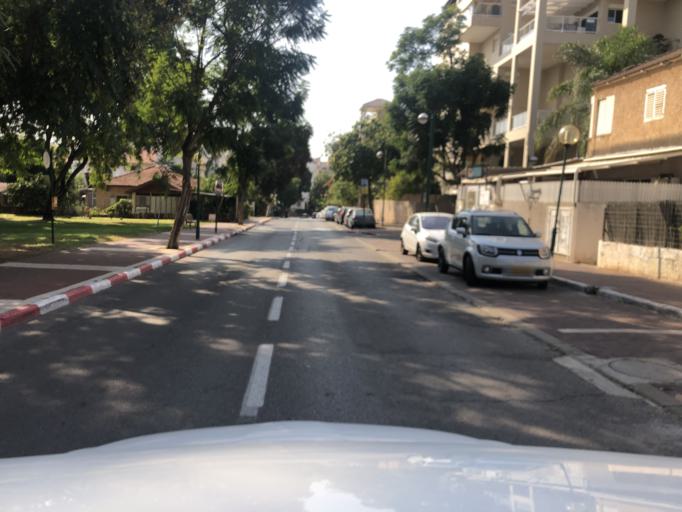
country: IL
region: Central District
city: Kfar Saba
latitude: 32.1806
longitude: 34.9067
